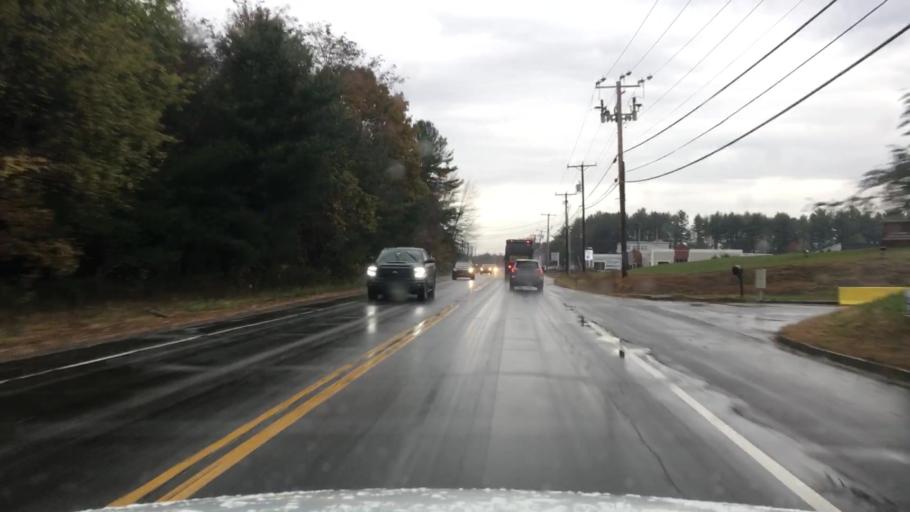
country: US
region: New Hampshire
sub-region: Strafford County
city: Somersworth
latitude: 43.2389
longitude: -70.8983
